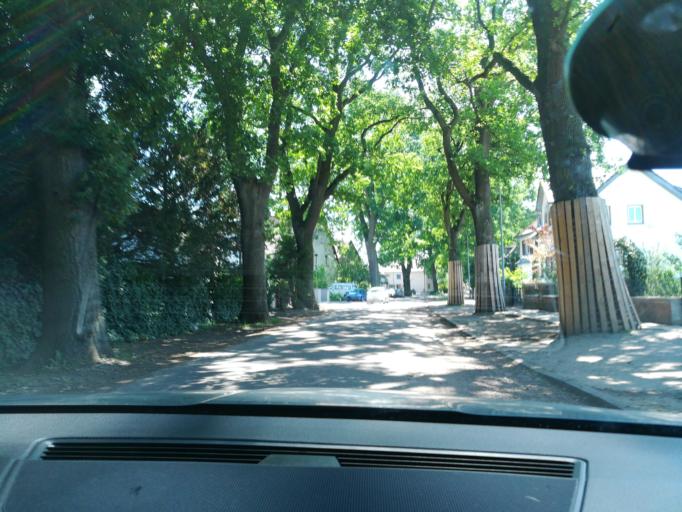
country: DE
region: North Rhine-Westphalia
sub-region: Regierungsbezirk Detmold
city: Minden
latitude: 52.3053
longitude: 8.9072
